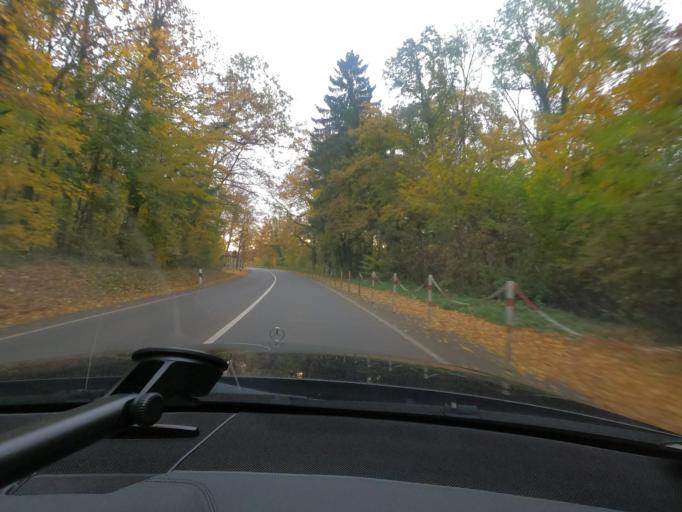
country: DE
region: North Rhine-Westphalia
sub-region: Regierungsbezirk Arnsberg
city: Mohnesee
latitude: 51.4788
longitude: 8.1795
